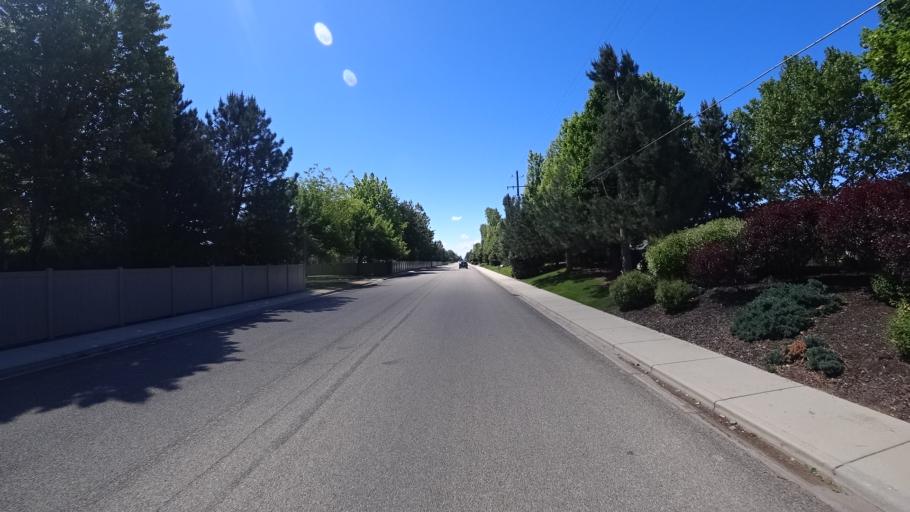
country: US
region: Idaho
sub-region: Ada County
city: Eagle
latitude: 43.6694
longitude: -116.3746
